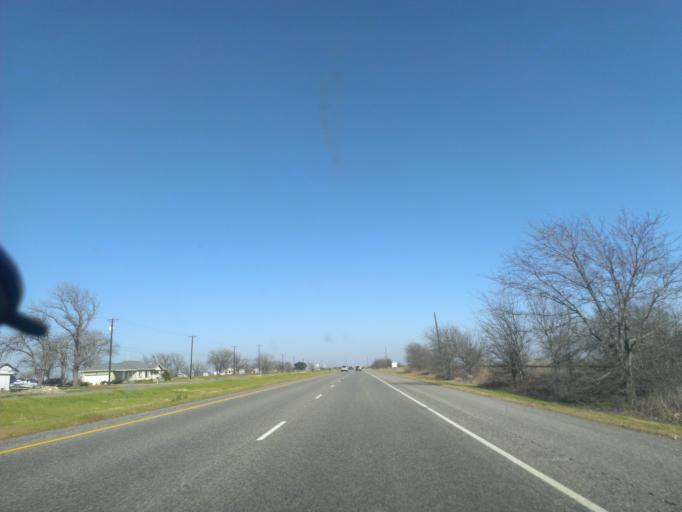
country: US
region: Texas
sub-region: Williamson County
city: Taylor
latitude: 30.5821
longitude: -97.3437
